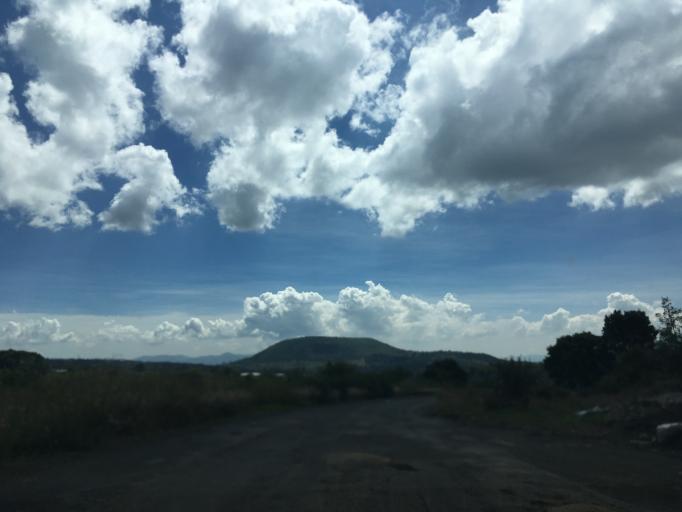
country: MX
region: Michoacan
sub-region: Morelia
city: Cuto de la Esperanza
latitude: 19.7332
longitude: -101.3495
